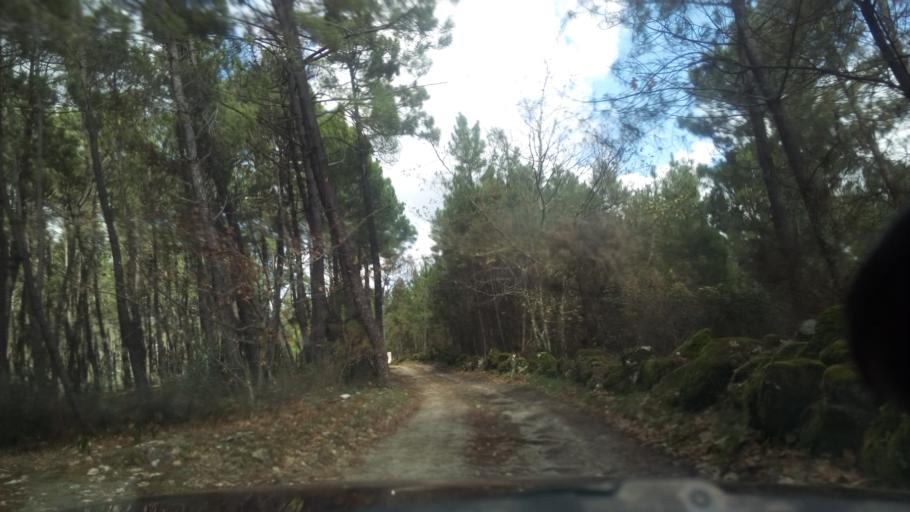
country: PT
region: Guarda
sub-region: Fornos de Algodres
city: Fornos de Algodres
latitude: 40.6252
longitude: -7.5238
